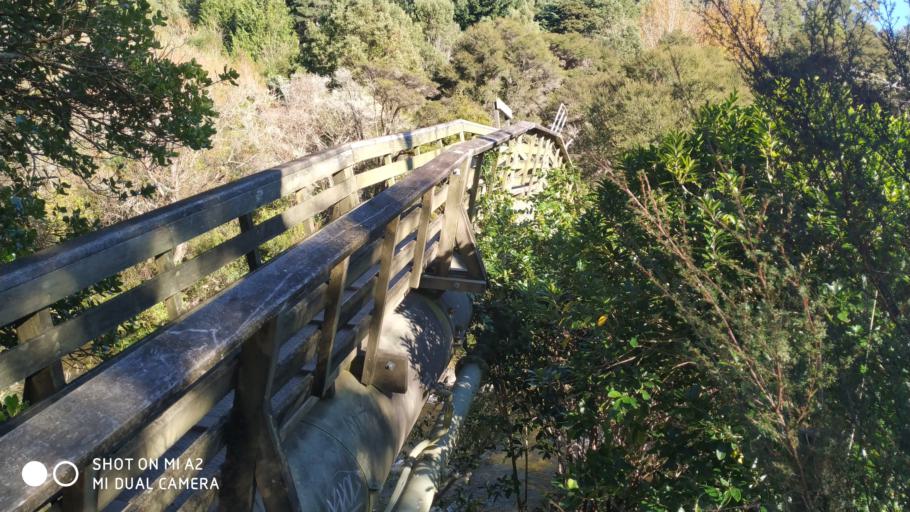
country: NZ
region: Nelson
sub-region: Nelson City
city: Nelson
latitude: -41.2927
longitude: 173.3241
